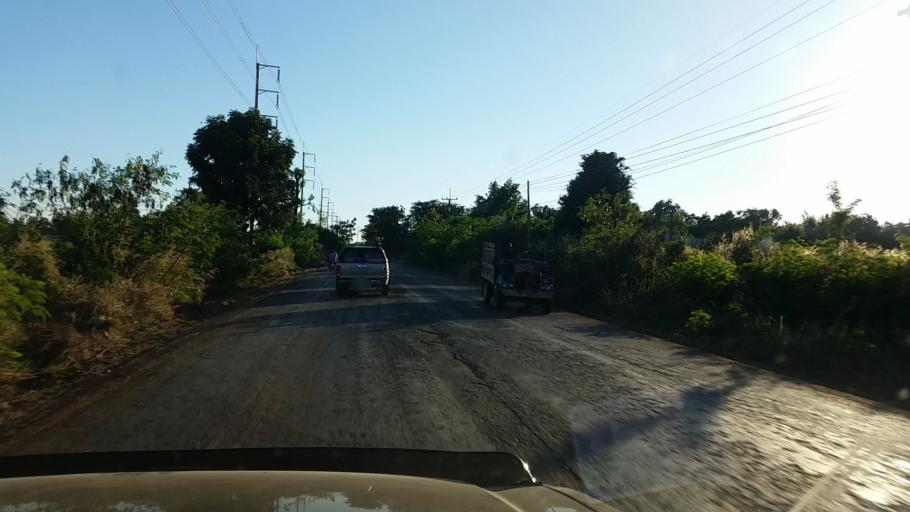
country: TH
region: Chaiyaphum
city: Nong Bua Rawe
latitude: 15.7395
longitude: 101.7554
